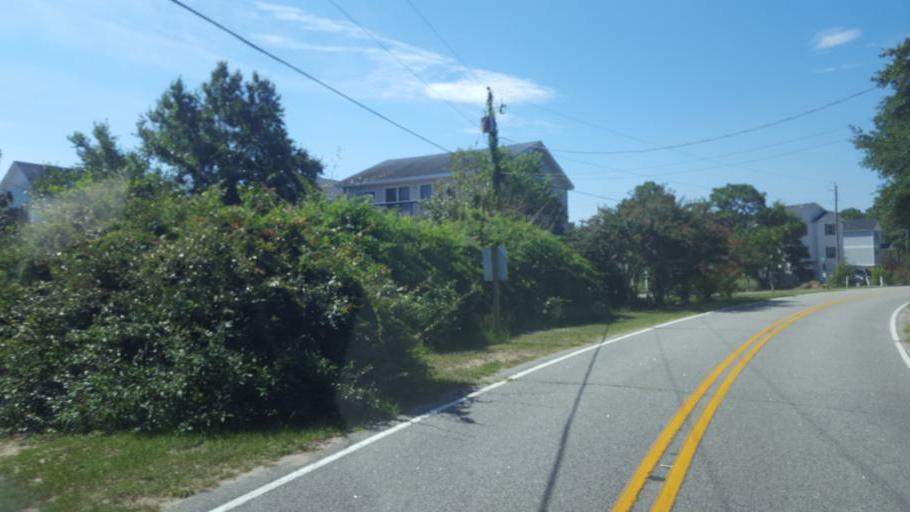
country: US
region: North Carolina
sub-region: Dare County
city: Kill Devil Hills
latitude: 36.0150
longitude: -75.7106
